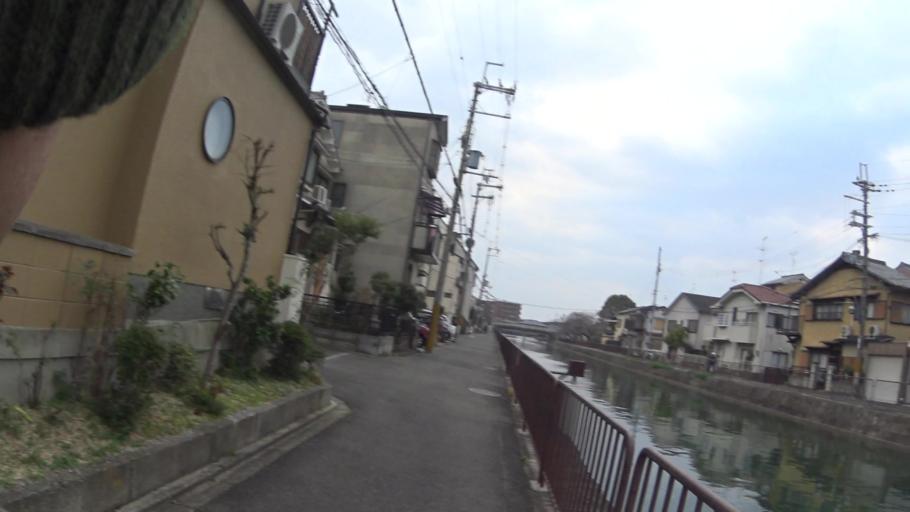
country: JP
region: Kyoto
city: Uji
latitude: 34.9471
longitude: 135.7683
